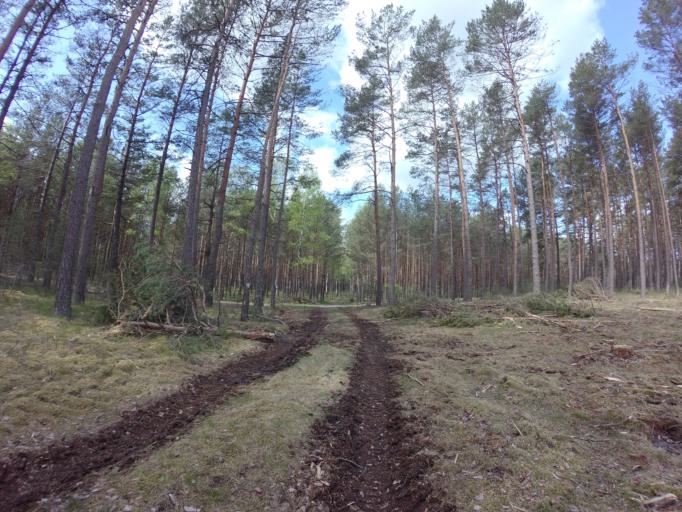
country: PL
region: West Pomeranian Voivodeship
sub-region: Powiat drawski
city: Kalisz Pomorski
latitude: 53.1944
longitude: 16.0002
